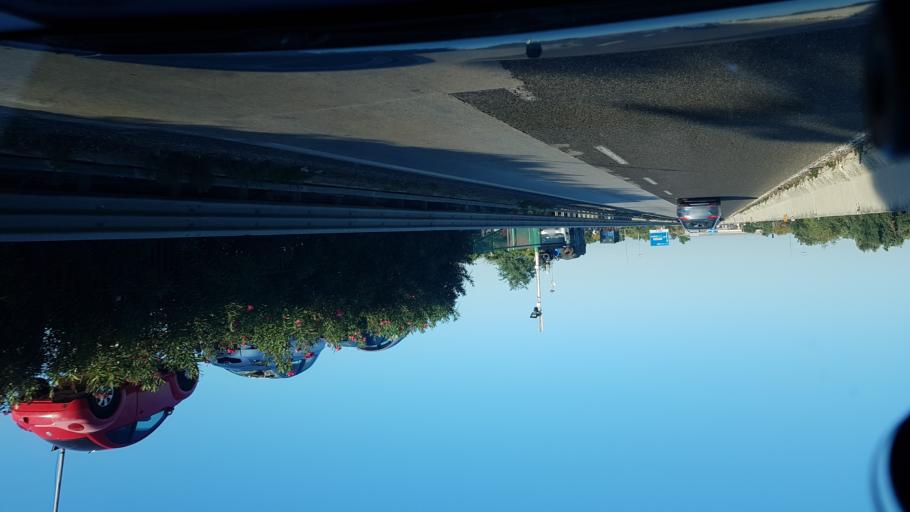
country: IT
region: Apulia
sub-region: Provincia di Brindisi
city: Fasano
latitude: 40.8466
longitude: 17.3620
